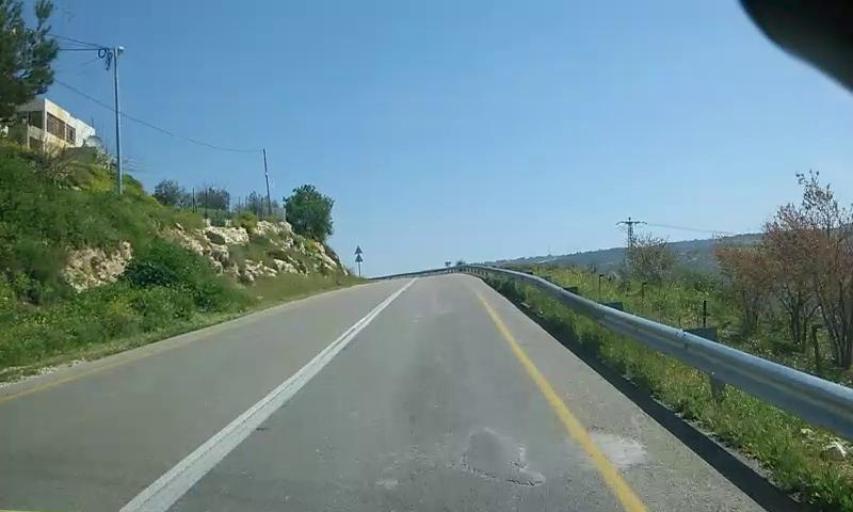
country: PS
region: West Bank
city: Surif
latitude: 31.6726
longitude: 35.0827
